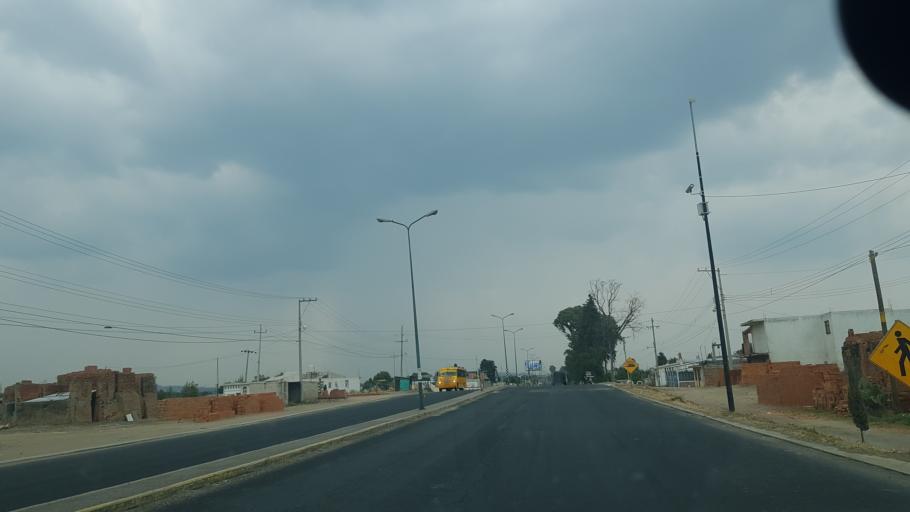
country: MX
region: Puebla
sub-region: Huejotzingo
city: San Mateo Capultitlan
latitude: 19.1809
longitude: -98.4163
